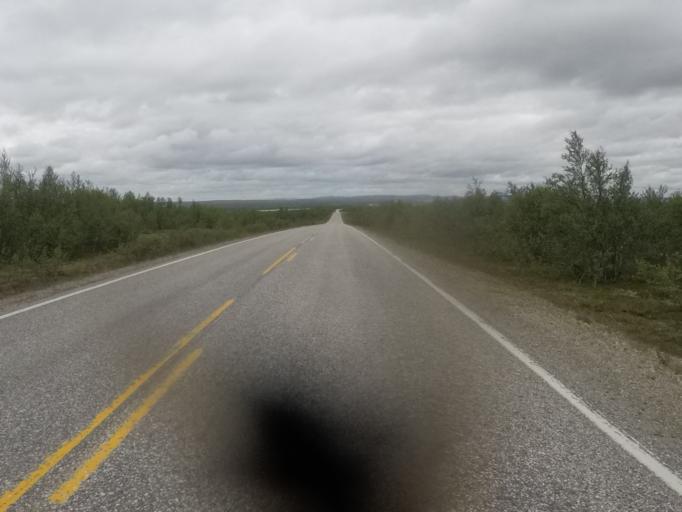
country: NO
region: Finnmark Fylke
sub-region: Kautokeino
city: Kautokeino
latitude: 68.7270
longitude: 23.3086
